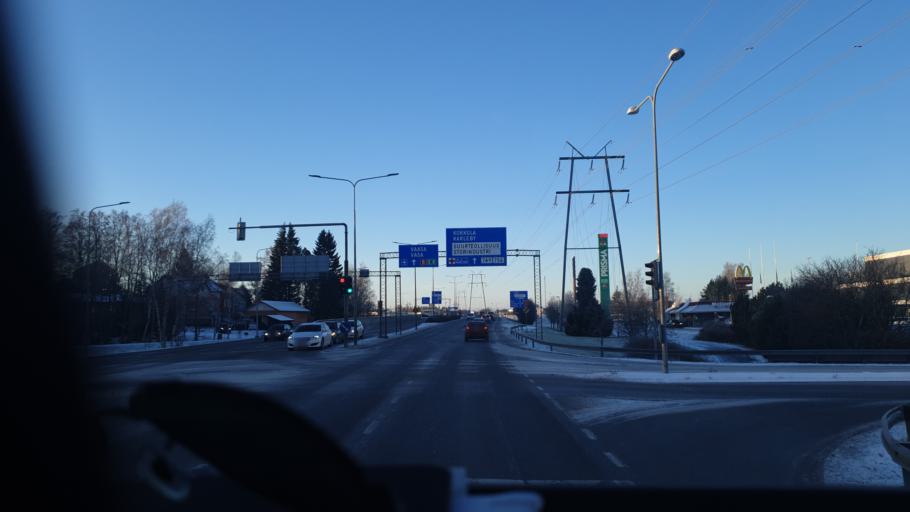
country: FI
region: Central Ostrobothnia
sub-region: Kokkola
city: Kokkola
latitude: 63.8312
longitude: 23.1276
